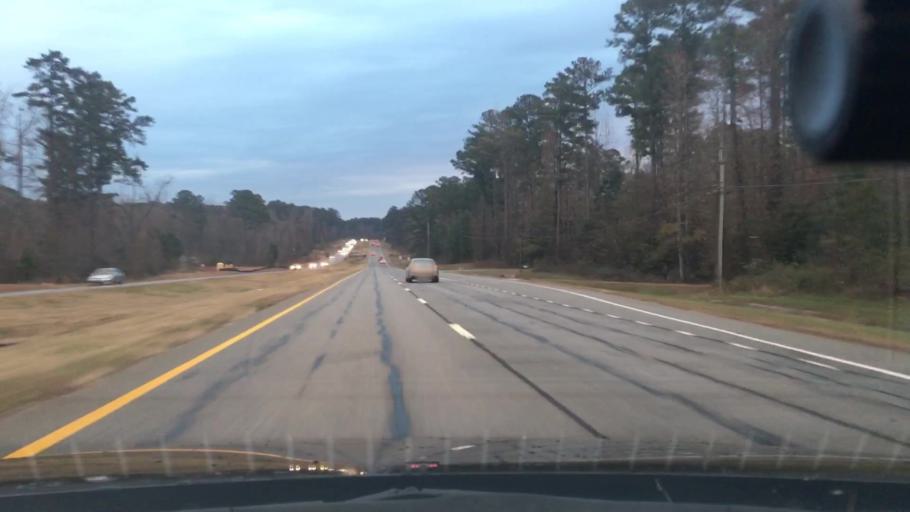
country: US
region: Georgia
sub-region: Fayette County
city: Peachtree City
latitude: 33.4016
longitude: -84.6454
